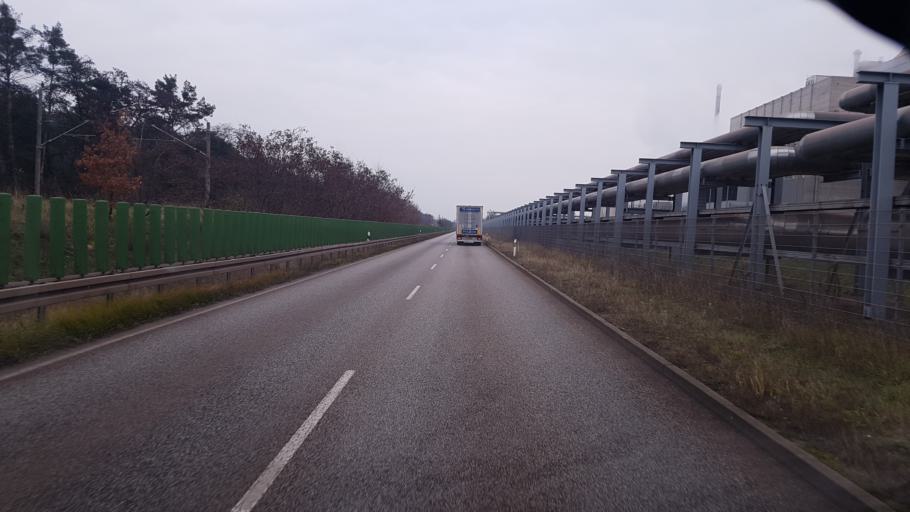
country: DE
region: Brandenburg
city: Vogelsang
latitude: 52.1752
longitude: 14.6403
